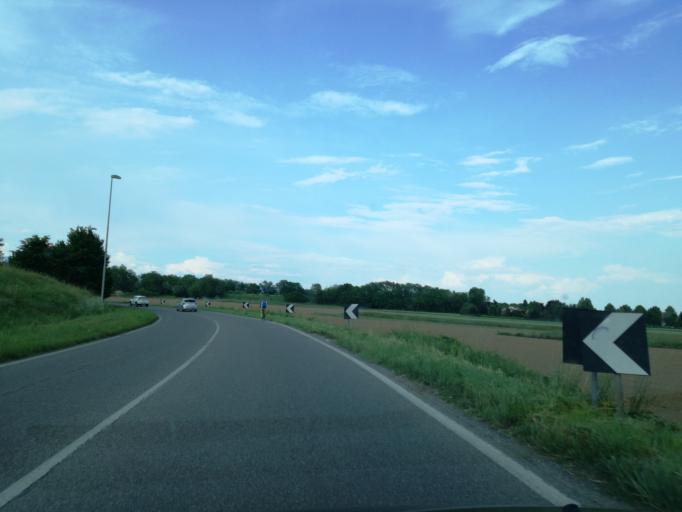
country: IT
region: Lombardy
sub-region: Provincia di Monza e Brianza
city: Vimercate
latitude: 45.6210
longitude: 9.3858
